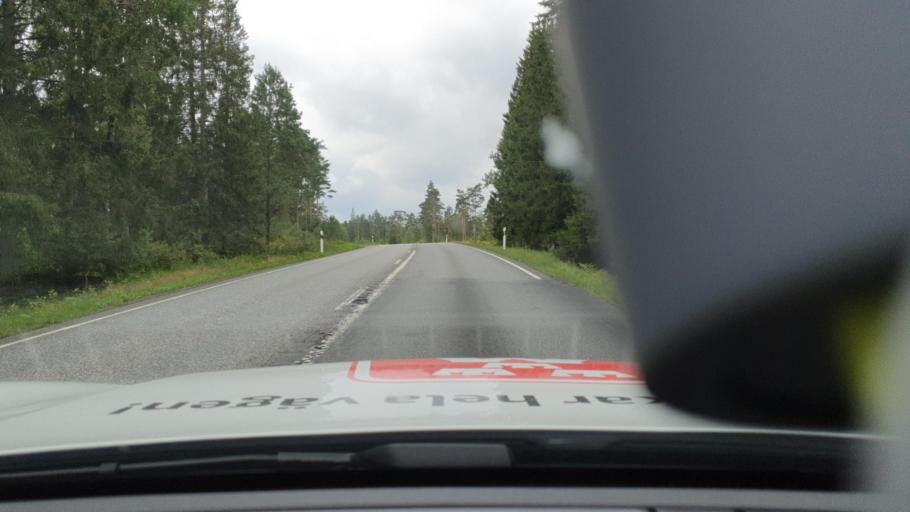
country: SE
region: Joenkoeping
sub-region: Gislaveds Kommun
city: Smalandsstenar
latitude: 57.2356
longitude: 13.4424
